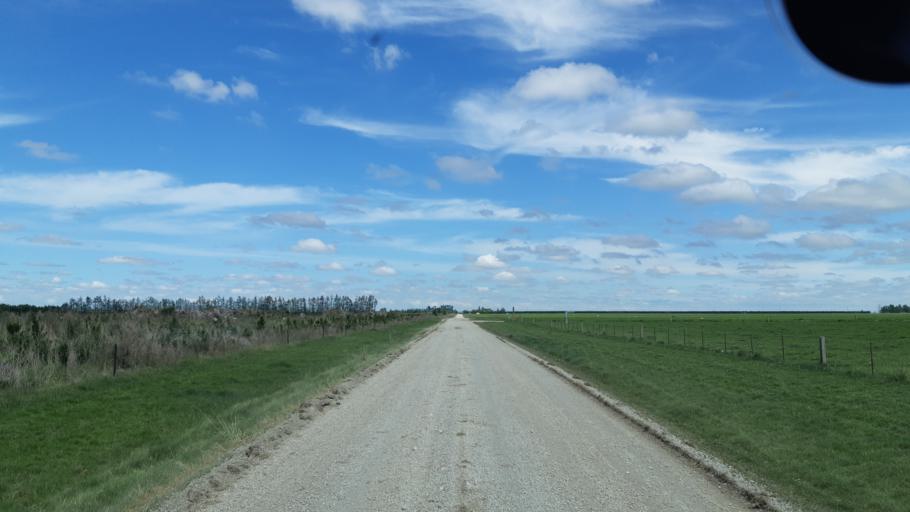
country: NZ
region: Canterbury
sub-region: Ashburton District
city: Methven
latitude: -43.7055
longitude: 171.4600
